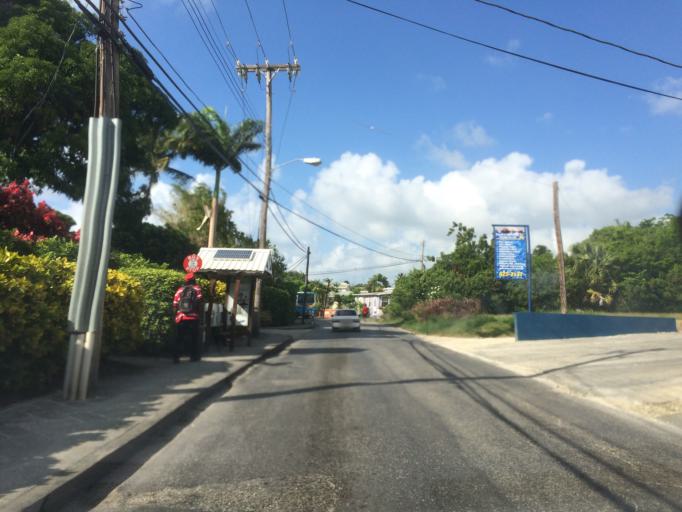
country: BB
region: Saint James
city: Holetown
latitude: 13.2121
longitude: -59.6397
